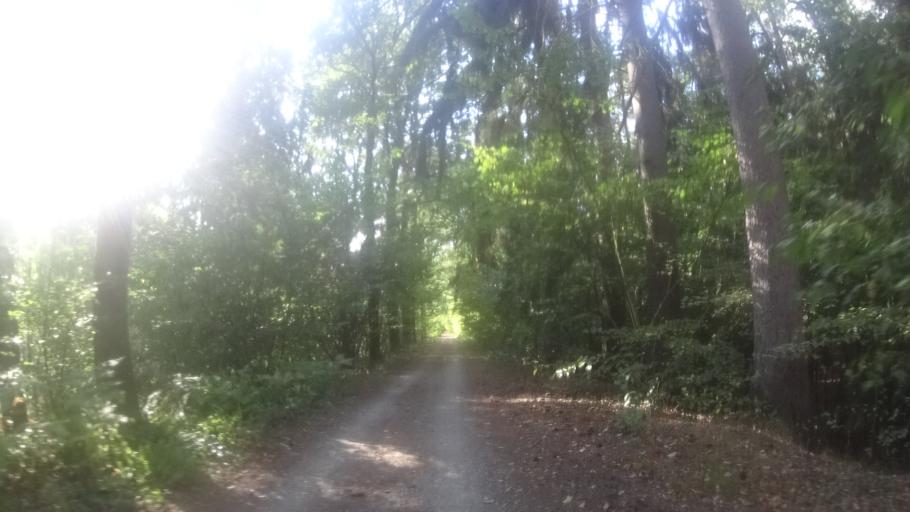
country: CZ
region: Kralovehradecky
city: Trebechovice pod Orebem
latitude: 50.1858
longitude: 16.0132
